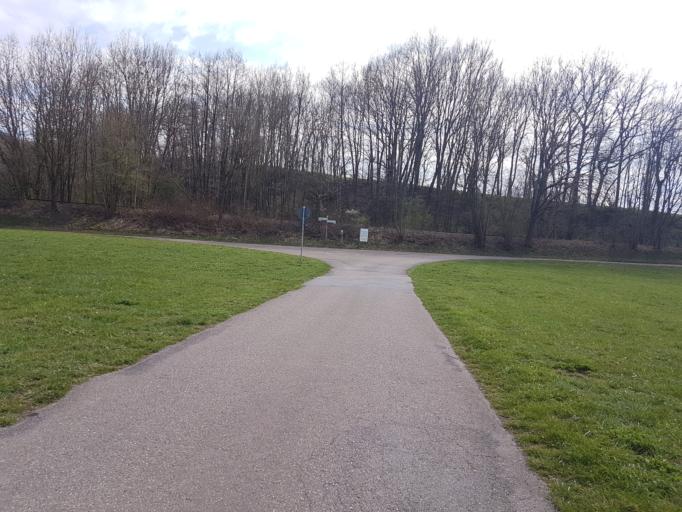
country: DE
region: Baden-Wuerttemberg
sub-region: Regierungsbezirk Stuttgart
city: Weissbach
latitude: 49.3550
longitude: 9.5741
